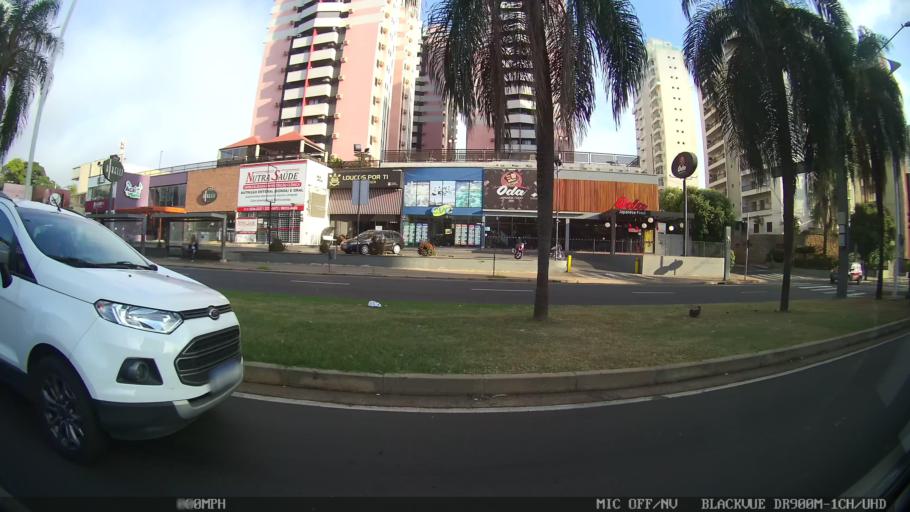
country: BR
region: Sao Paulo
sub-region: Sao Jose Do Rio Preto
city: Sao Jose do Rio Preto
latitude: -20.8215
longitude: -49.3839
